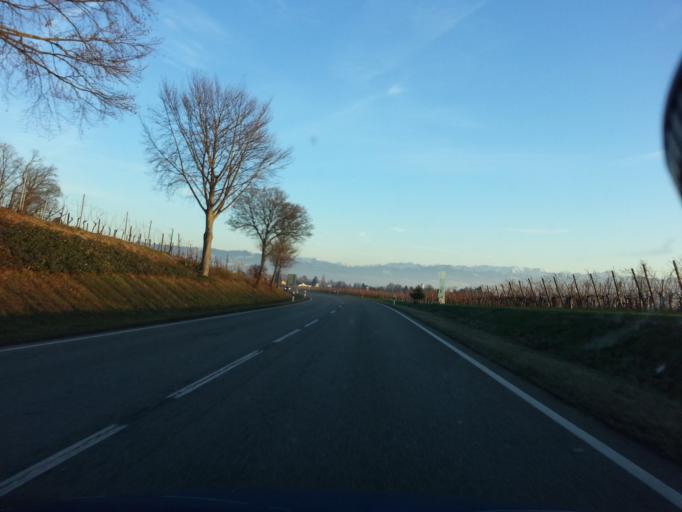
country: DE
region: Bavaria
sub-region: Swabia
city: Nonnenhorn
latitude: 47.5773
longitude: 9.6163
